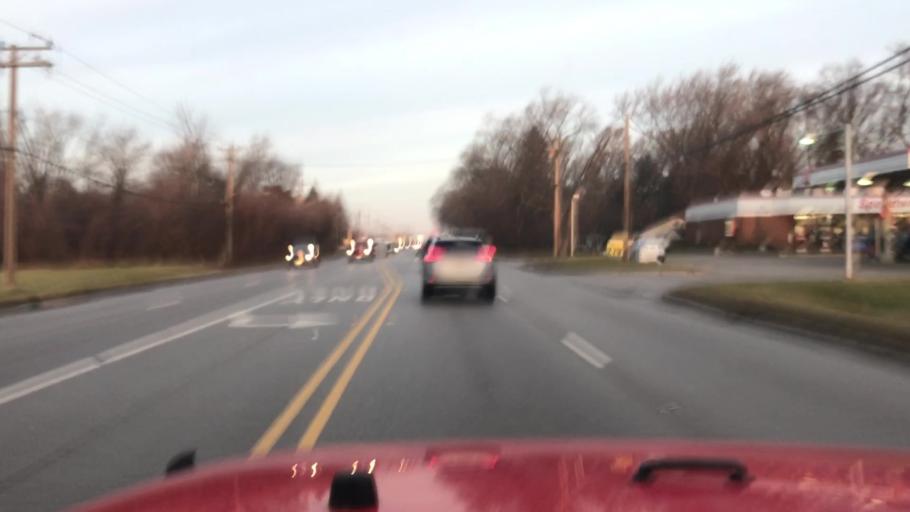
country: US
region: Illinois
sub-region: Cook County
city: Prospect Heights
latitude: 42.0966
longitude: -87.9565
